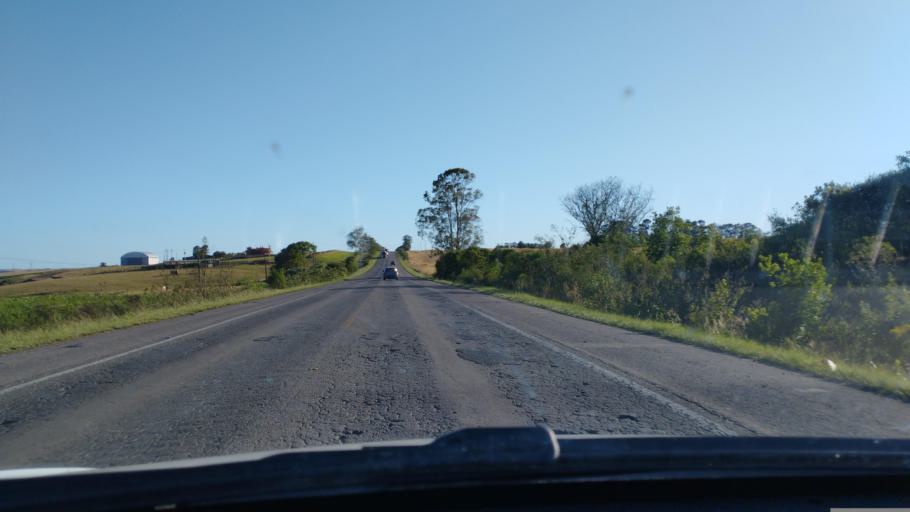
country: BR
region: Rio Grande do Sul
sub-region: Julio De Castilhos
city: Julio de Castilhos
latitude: -29.4206
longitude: -53.6721
